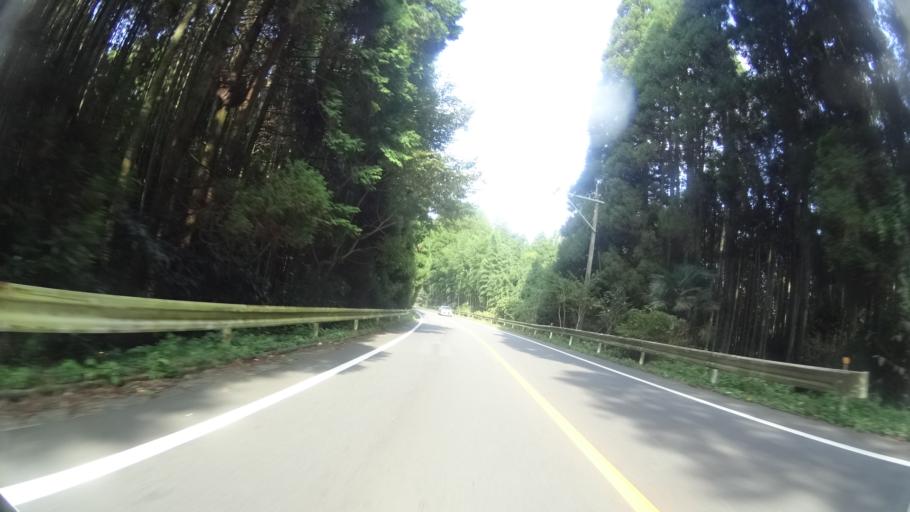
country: JP
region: Kumamoto
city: Aso
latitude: 33.0835
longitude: 131.0648
